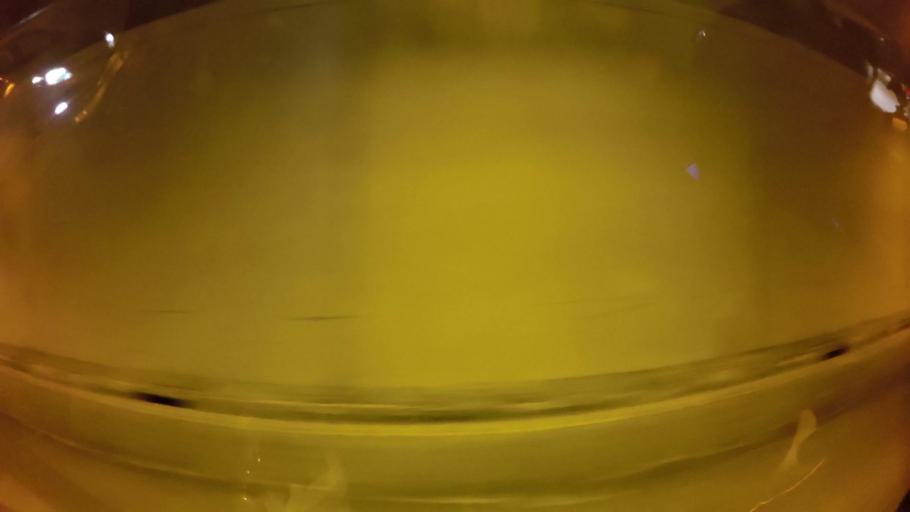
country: EC
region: Guayas
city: Eloy Alfaro
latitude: -2.1817
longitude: -79.8807
